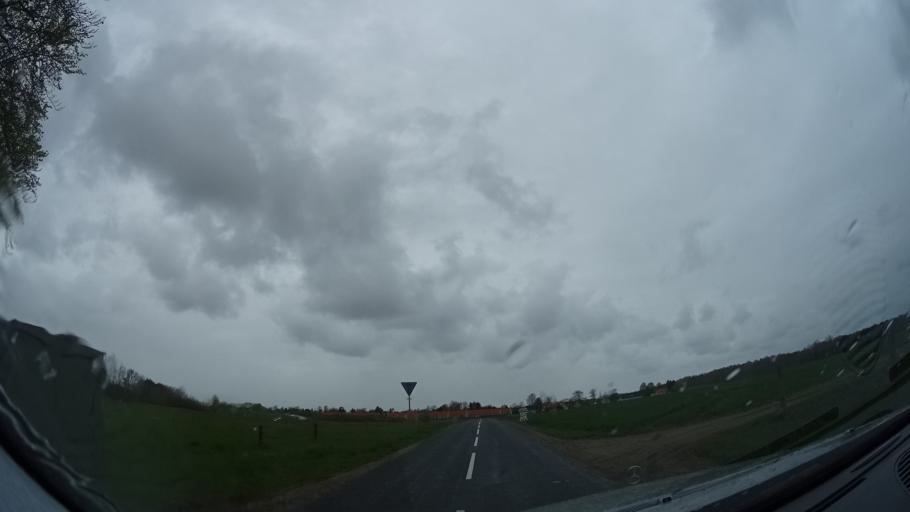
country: DK
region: Zealand
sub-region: Holbaek Kommune
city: Vipperod
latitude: 55.7010
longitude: 11.7795
